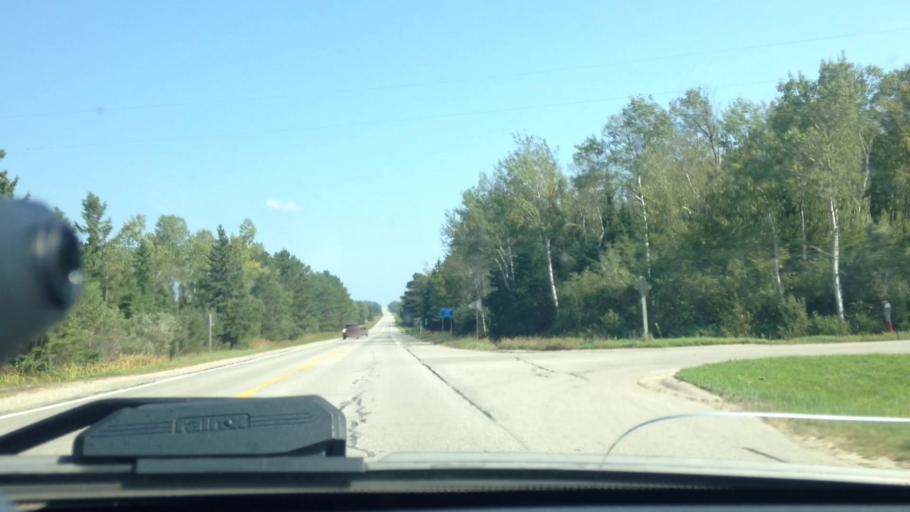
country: US
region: Michigan
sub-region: Luce County
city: Newberry
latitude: 46.3105
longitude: -85.5941
